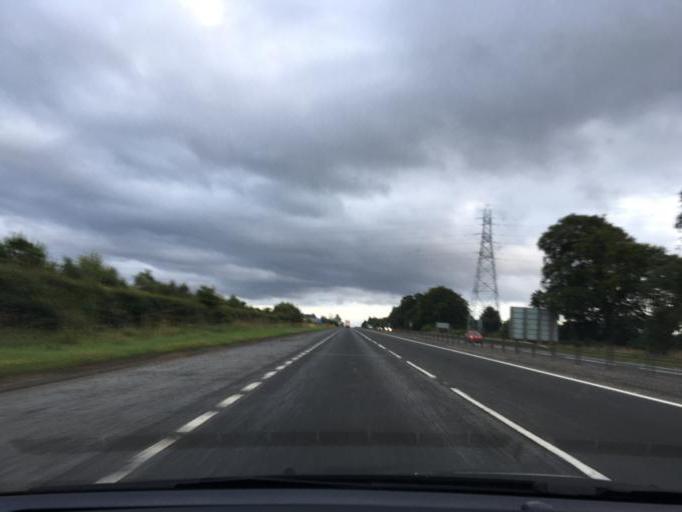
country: GB
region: Scotland
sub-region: Highland
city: Inverness
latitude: 57.4513
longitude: -4.1582
